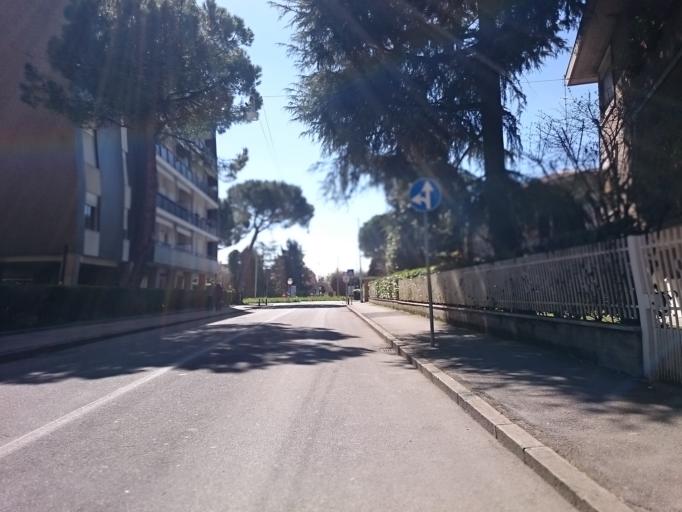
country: IT
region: Veneto
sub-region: Provincia di Padova
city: Padova
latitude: 45.3929
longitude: 11.8857
